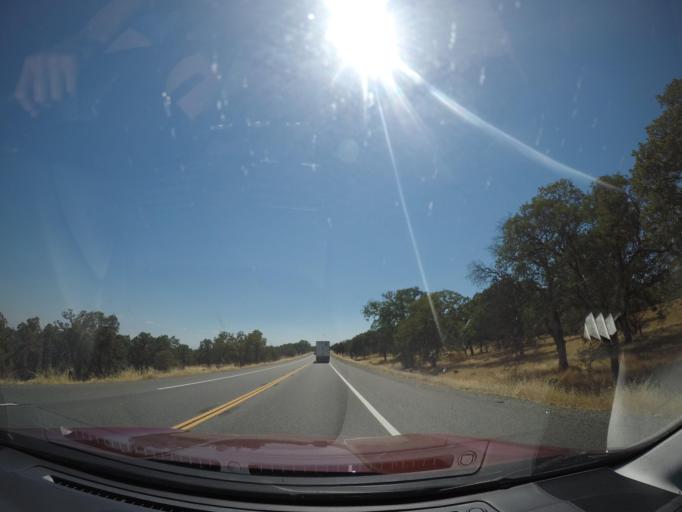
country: US
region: California
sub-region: Shasta County
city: Bella Vista
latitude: 40.6950
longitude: -122.1060
